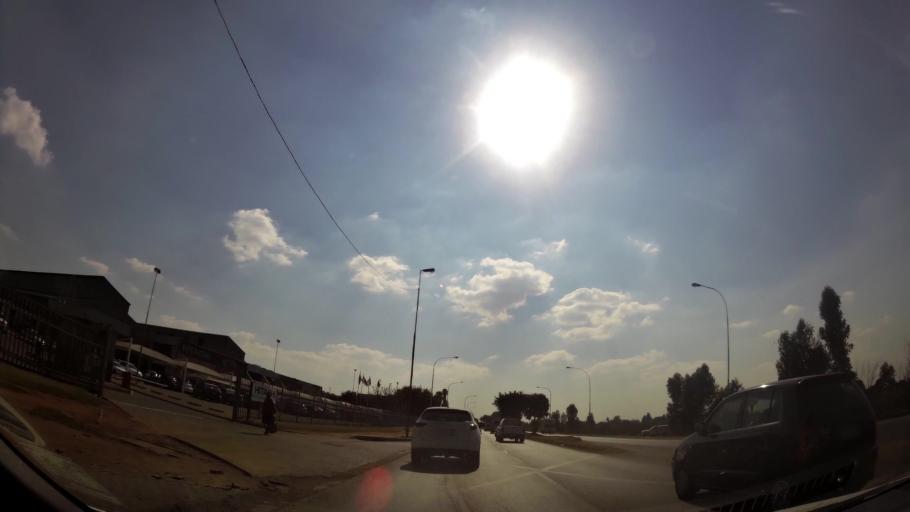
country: ZA
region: Gauteng
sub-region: Ekurhuleni Metropolitan Municipality
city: Boksburg
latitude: -26.2018
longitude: 28.2837
